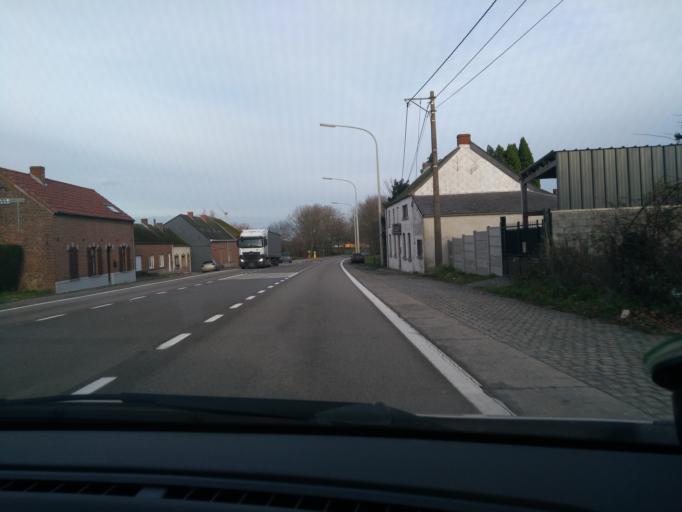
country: BE
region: Wallonia
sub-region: Province du Hainaut
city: Quevy-le-Petit
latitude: 50.3557
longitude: 3.9674
